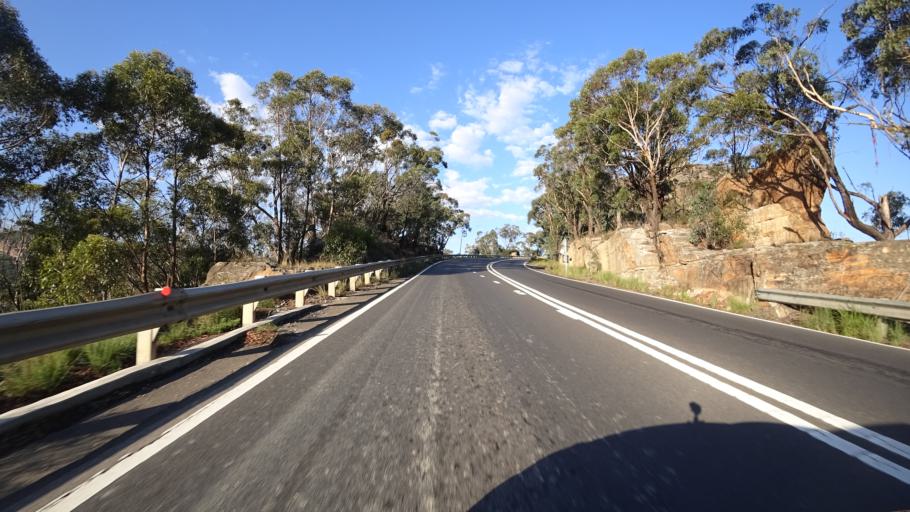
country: AU
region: New South Wales
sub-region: Blue Mountains Municipality
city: Blackheath
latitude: -33.5818
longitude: 150.2324
